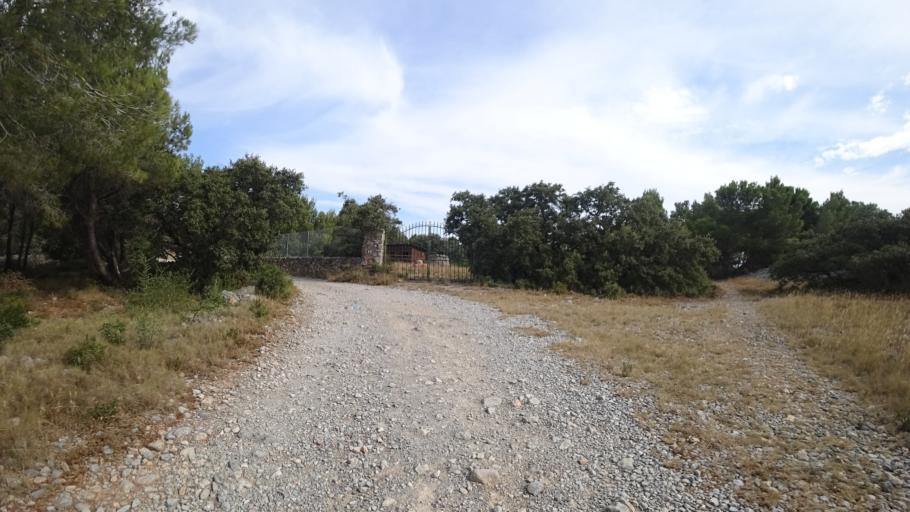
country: FR
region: Languedoc-Roussillon
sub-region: Departement de l'Aude
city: Leucate
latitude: 42.8991
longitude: 3.0354
